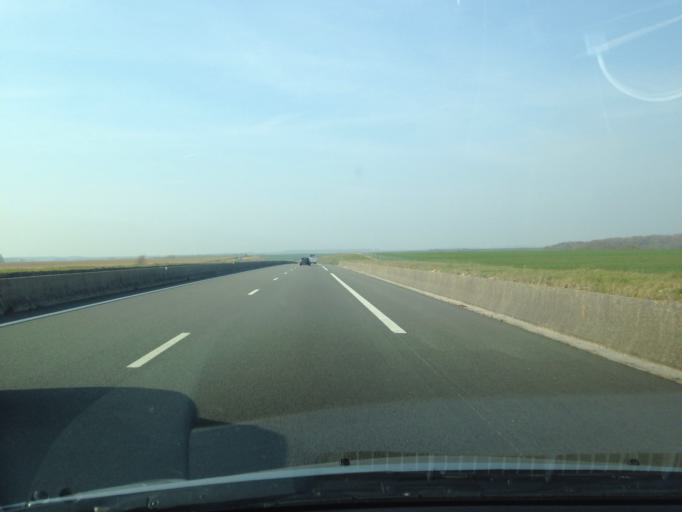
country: FR
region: Picardie
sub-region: Departement de la Somme
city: Rue
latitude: 50.3148
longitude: 1.7222
